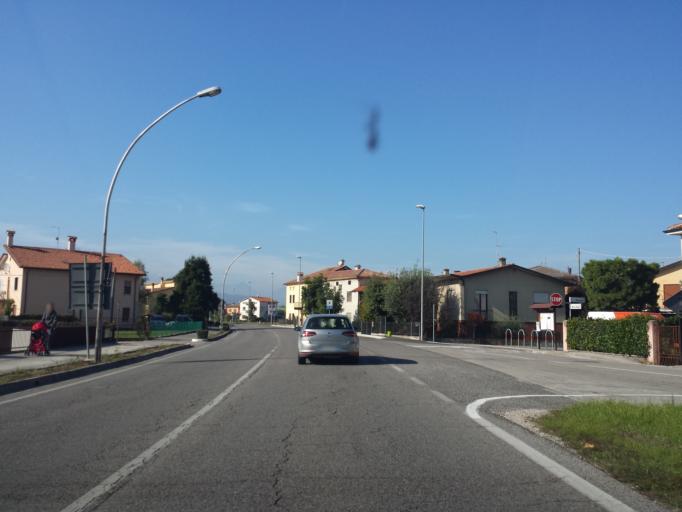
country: IT
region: Veneto
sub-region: Provincia di Vicenza
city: Motta
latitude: 45.6045
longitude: 11.4920
